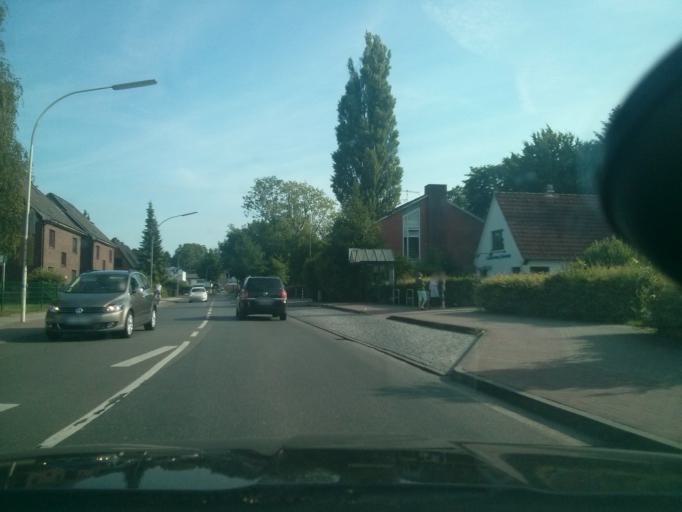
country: DE
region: Schleswig-Holstein
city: Halstenbek
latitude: 53.6002
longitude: 9.8380
